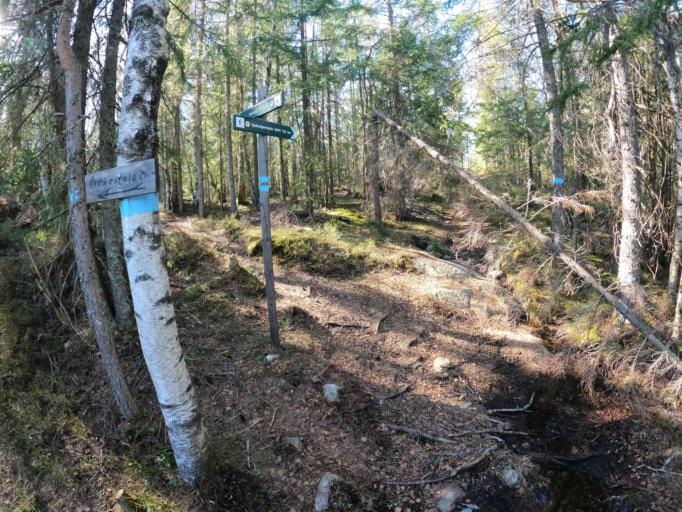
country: NO
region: Akershus
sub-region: Gjerdrum
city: Ask
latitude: 60.0621
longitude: 10.9519
